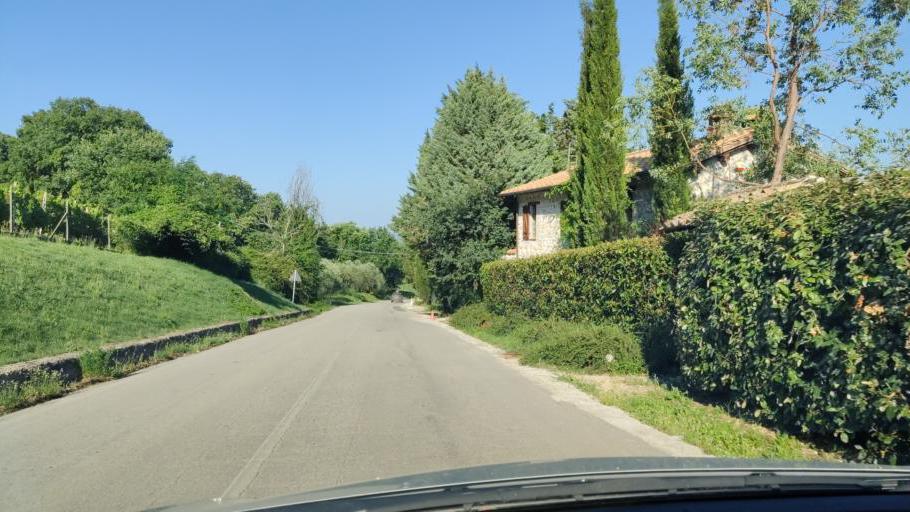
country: IT
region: Umbria
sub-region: Provincia di Terni
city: Penna in Teverina
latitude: 42.4880
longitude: 12.3593
